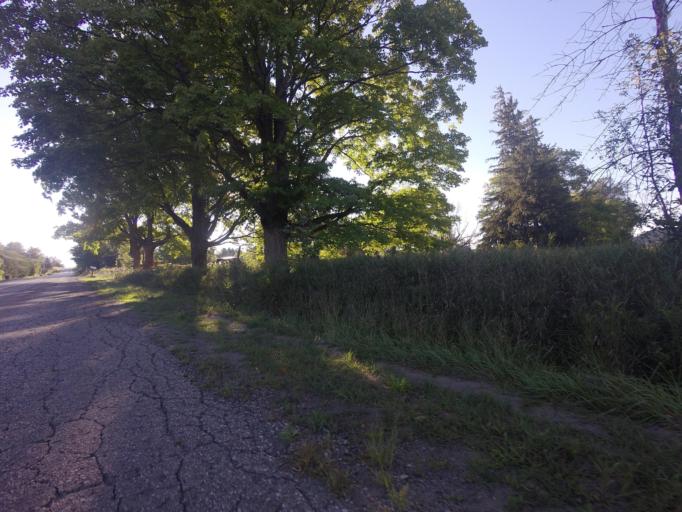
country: CA
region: Ontario
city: Bradford West Gwillimbury
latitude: 44.0402
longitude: -79.7826
